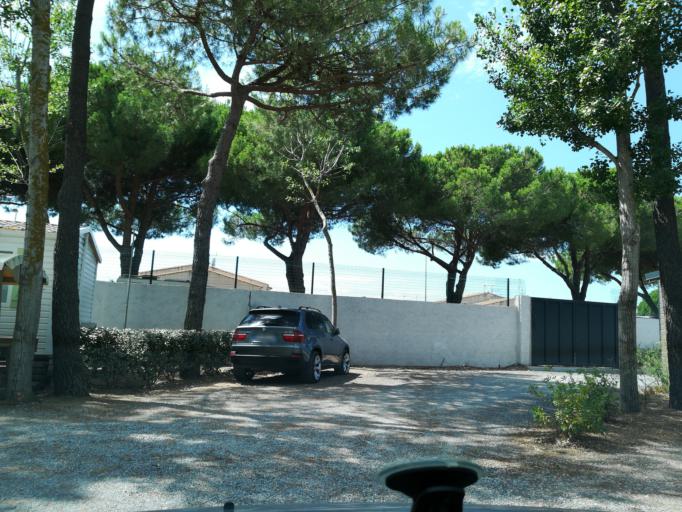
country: FR
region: Languedoc-Roussillon
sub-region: Departement de l'Herault
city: Portiragnes
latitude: 43.2825
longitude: 3.3635
